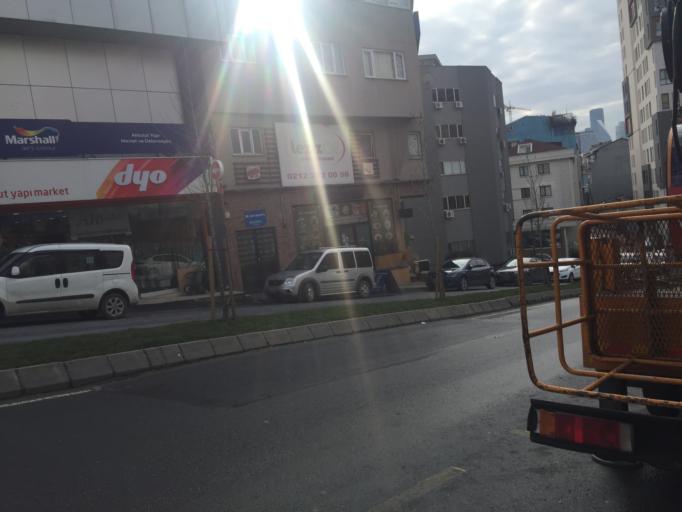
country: TR
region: Istanbul
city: Sisli
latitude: 41.0994
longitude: 28.9979
